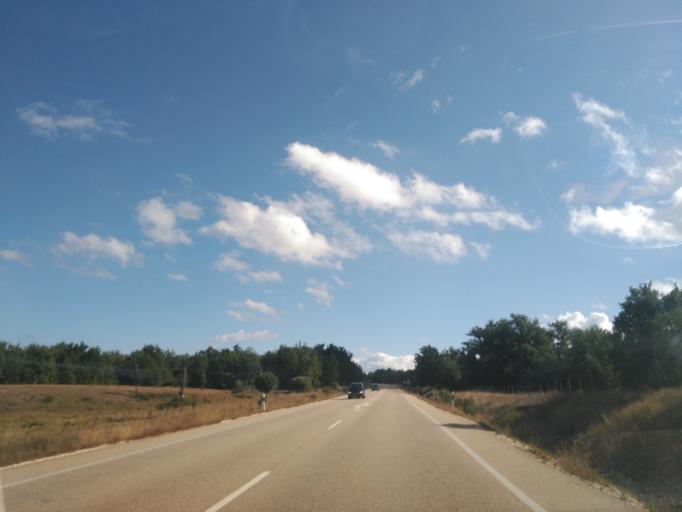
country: ES
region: Castille and Leon
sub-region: Provincia de Burgos
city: Pinilla de los Barruecos
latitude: 41.9324
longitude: -3.2833
